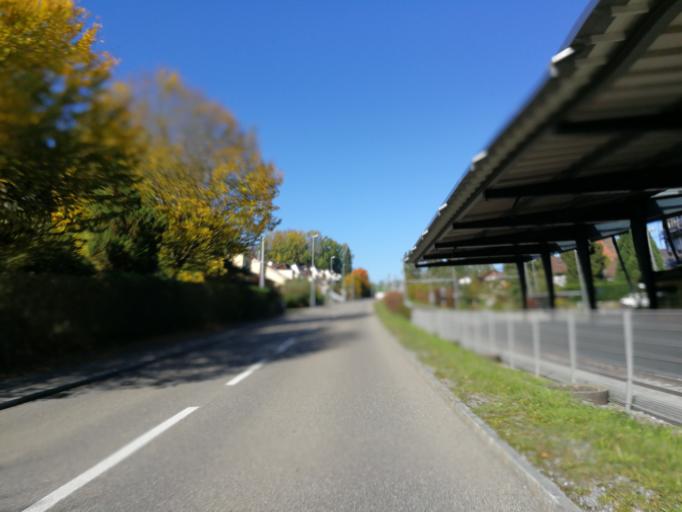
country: CH
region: Zurich
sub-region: Bezirk Uster
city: Esslingen
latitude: 47.2878
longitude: 8.7096
